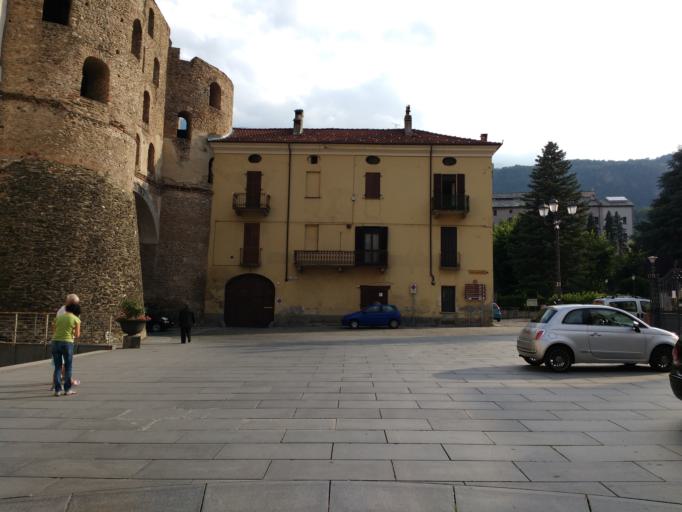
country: IT
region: Piedmont
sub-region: Provincia di Torino
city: San Giuseppe
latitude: 45.1372
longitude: 7.0446
